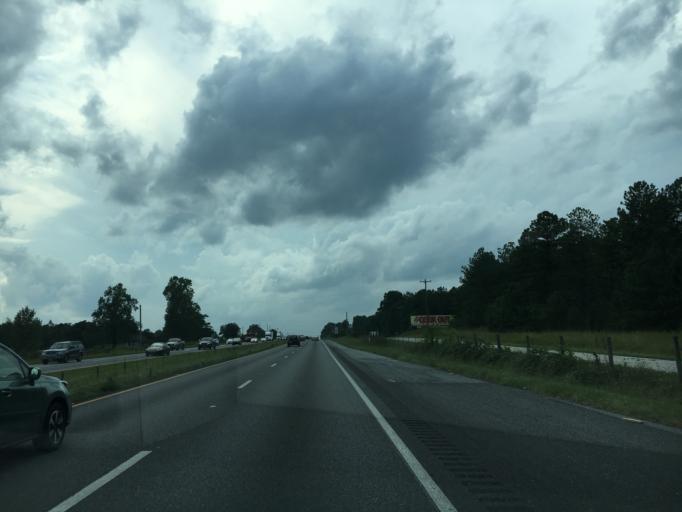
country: US
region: South Carolina
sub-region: Cherokee County
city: Gaffney
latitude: 35.0760
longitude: -81.7345
